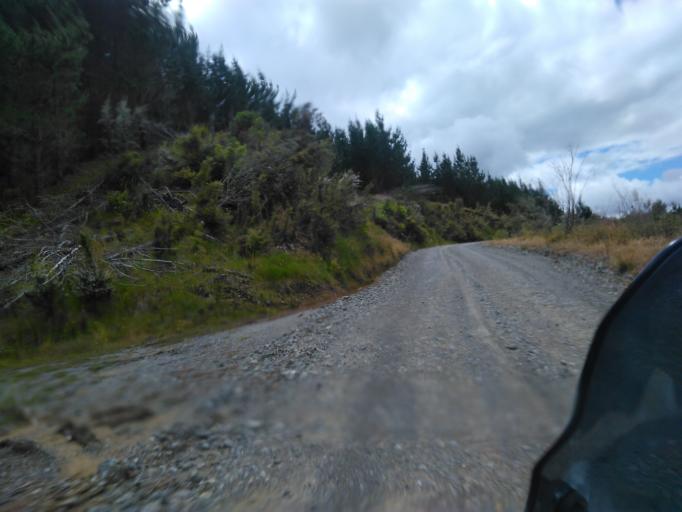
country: NZ
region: Gisborne
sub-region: Gisborne District
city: Gisborne
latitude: -38.1854
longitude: 178.1073
